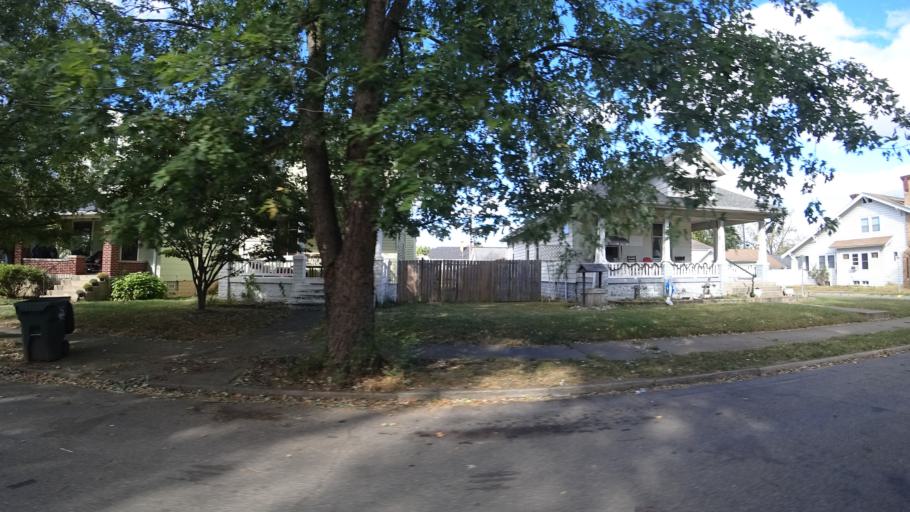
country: US
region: Ohio
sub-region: Butler County
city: Fairfield
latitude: 39.3685
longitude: -84.5557
